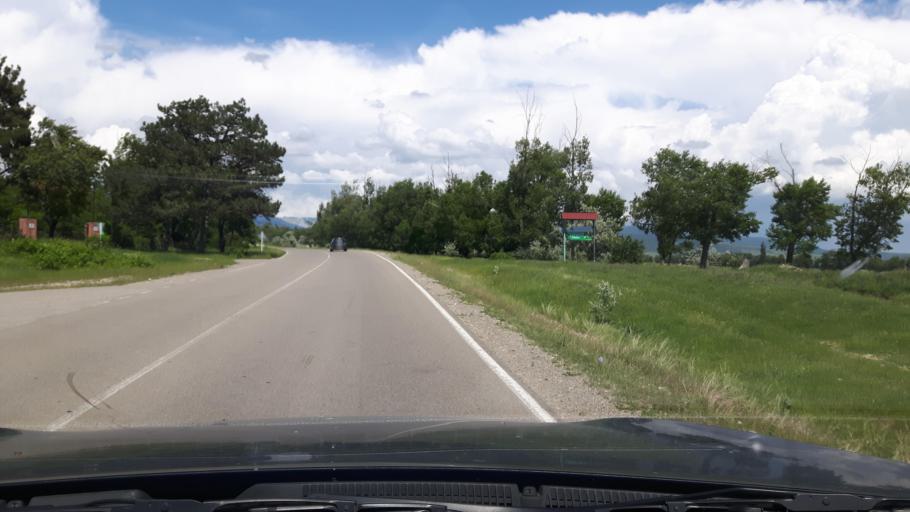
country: GE
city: Didi Lilo
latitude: 41.7389
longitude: 45.1256
